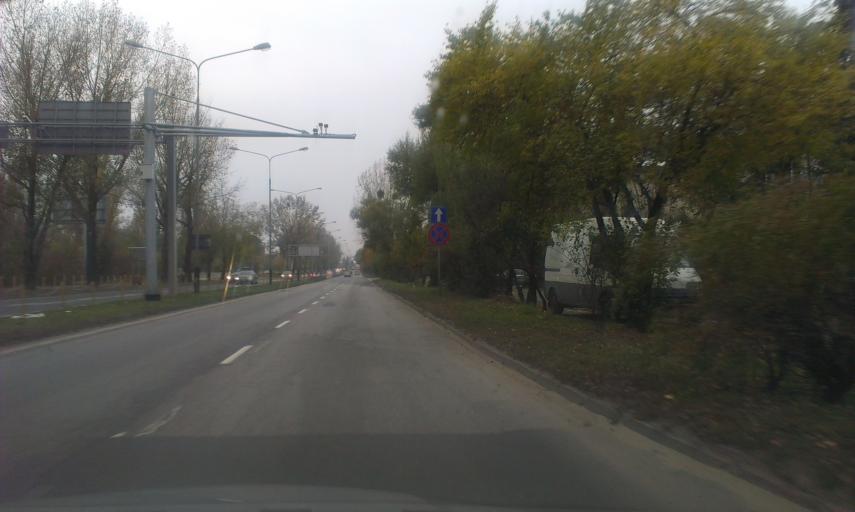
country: PL
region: Greater Poland Voivodeship
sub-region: Powiat poznanski
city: Suchy Las
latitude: 52.4228
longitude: 16.8687
